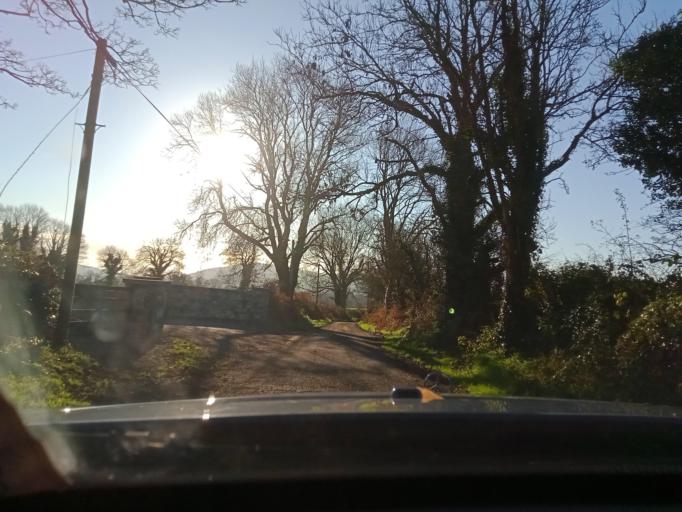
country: IE
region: Munster
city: Carrick-on-Suir
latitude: 52.4469
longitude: -7.4172
